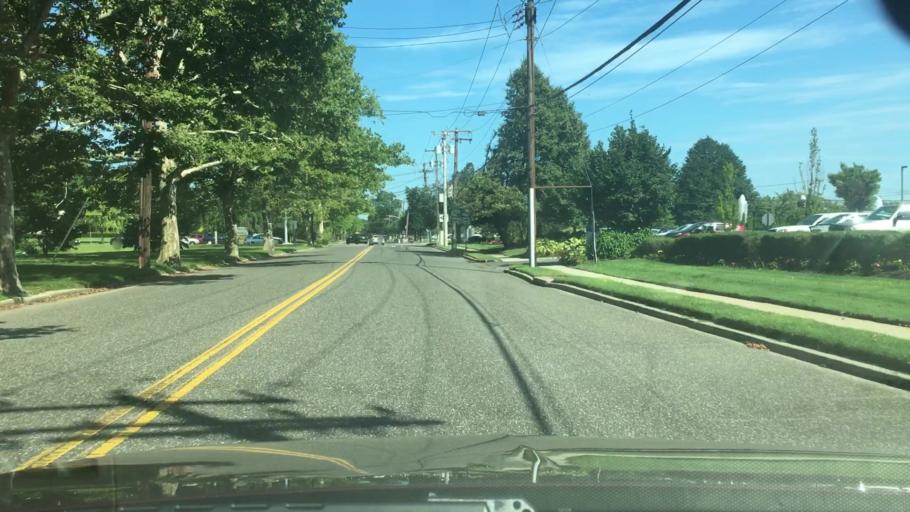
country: US
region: New York
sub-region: Suffolk County
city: Melville
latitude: 40.7729
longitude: -73.4237
